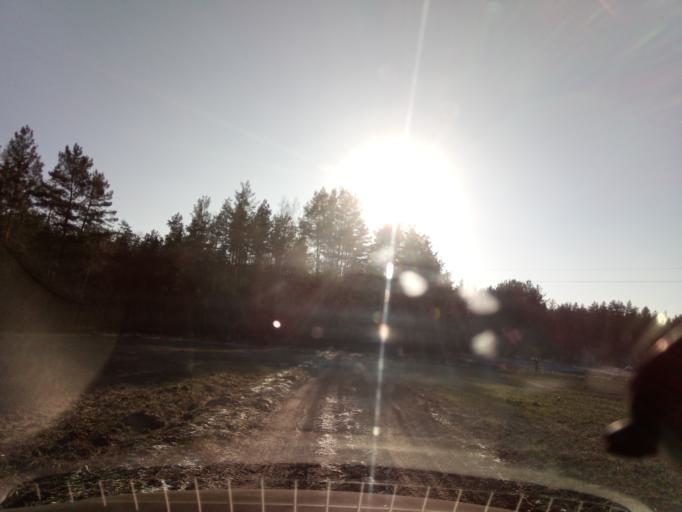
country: LT
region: Alytaus apskritis
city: Druskininkai
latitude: 53.9818
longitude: 23.8979
